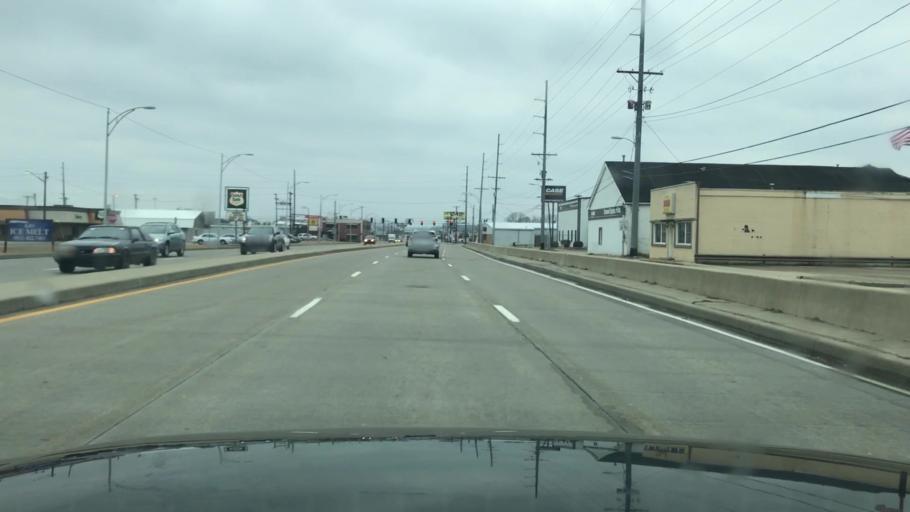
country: US
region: Indiana
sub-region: Vanderburgh County
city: Evansville
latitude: 37.9992
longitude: -87.5445
